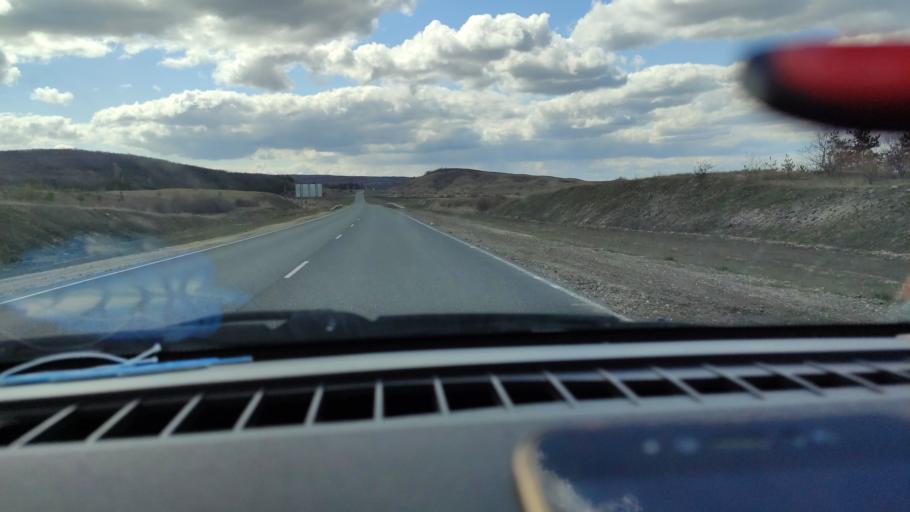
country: RU
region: Saratov
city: Alekseyevka
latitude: 52.3785
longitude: 47.9721
